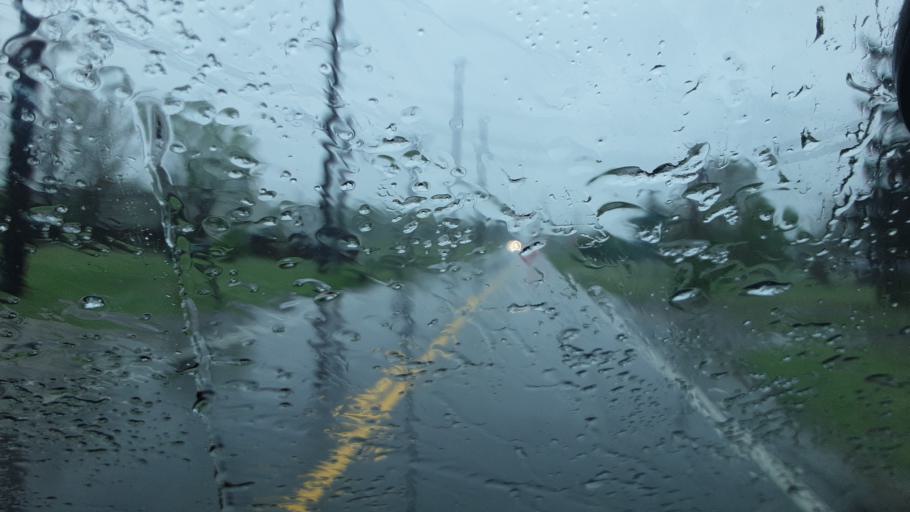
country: US
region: Ohio
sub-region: Portage County
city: Windham
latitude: 41.3085
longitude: -80.9701
